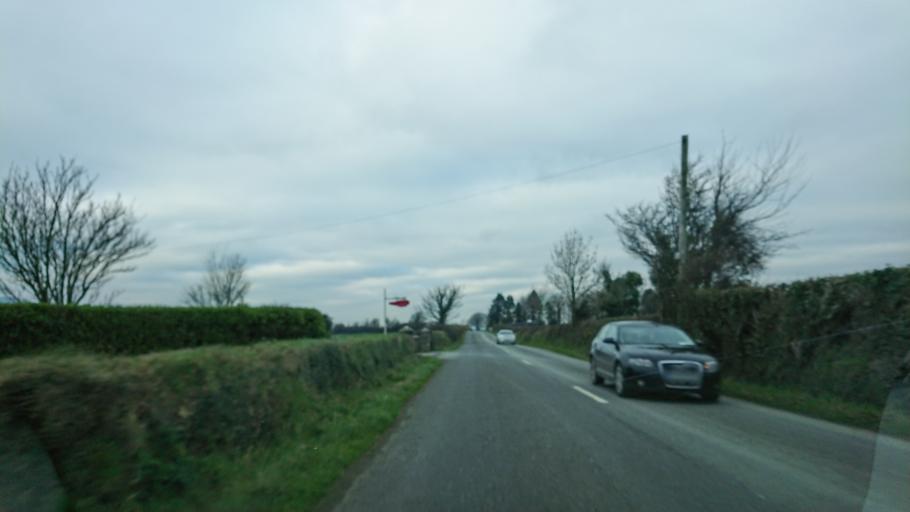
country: IE
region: Munster
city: Carrick-on-Suir
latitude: 52.2932
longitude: -7.4676
